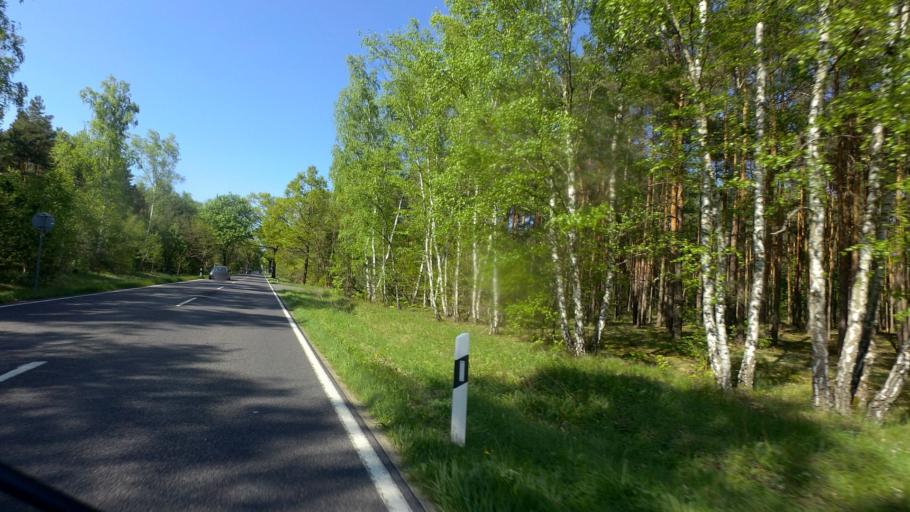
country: DE
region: Brandenburg
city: Gross Koris
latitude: 52.1919
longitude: 13.6974
